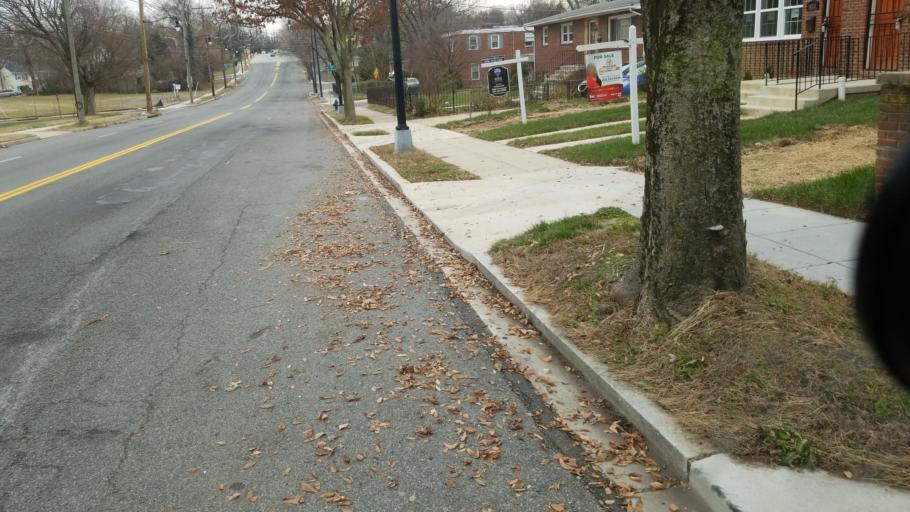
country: US
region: Maryland
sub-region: Prince George's County
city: Fairmount Heights
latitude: 38.9002
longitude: -76.9188
